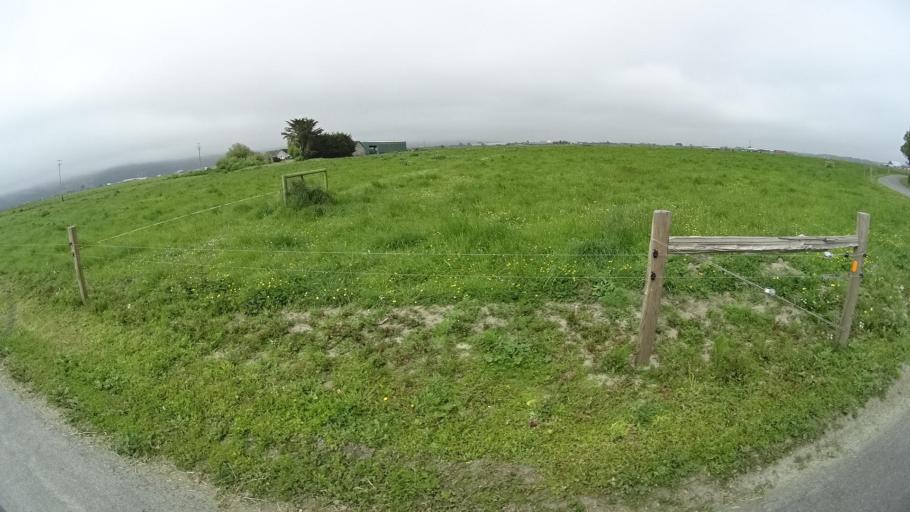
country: US
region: California
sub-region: Humboldt County
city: Fortuna
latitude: 40.5898
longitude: -124.1874
